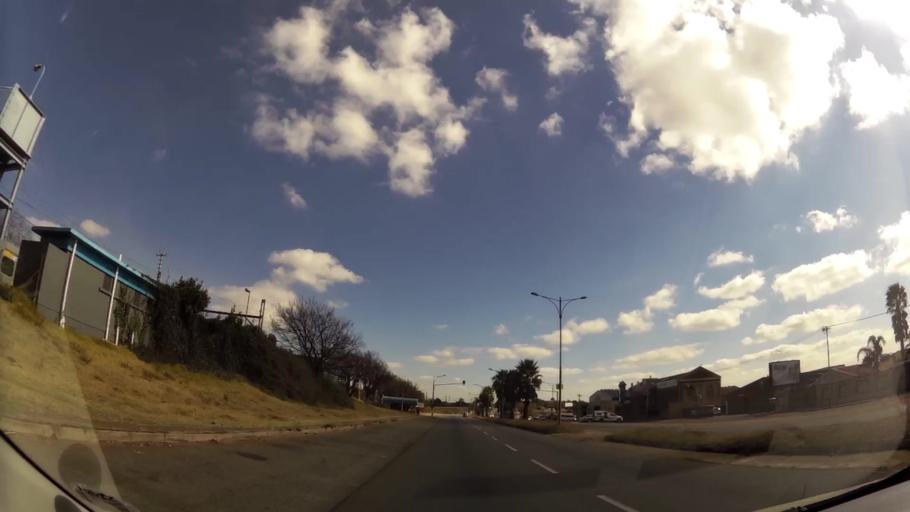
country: ZA
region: Gauteng
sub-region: City of Johannesburg Metropolitan Municipality
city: Roodepoort
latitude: -26.1270
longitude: 27.8311
